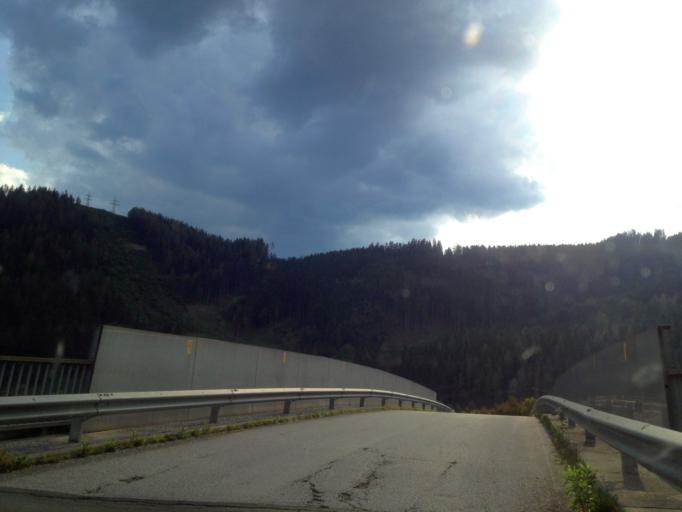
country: AT
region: Styria
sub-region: Politischer Bezirk Leoben
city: Sankt Michael in Obersteiermark
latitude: 47.3554
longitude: 15.0054
